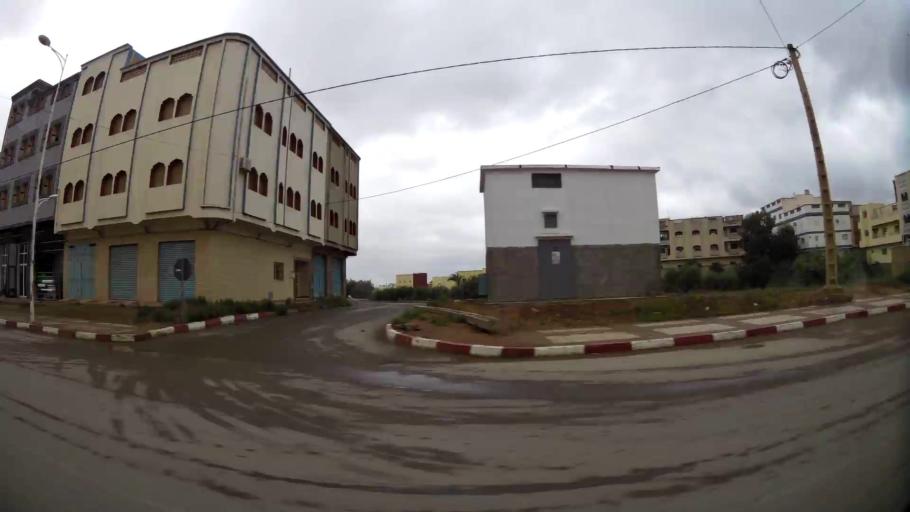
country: MA
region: Oriental
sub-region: Nador
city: Midar
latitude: 35.0489
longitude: -3.4581
